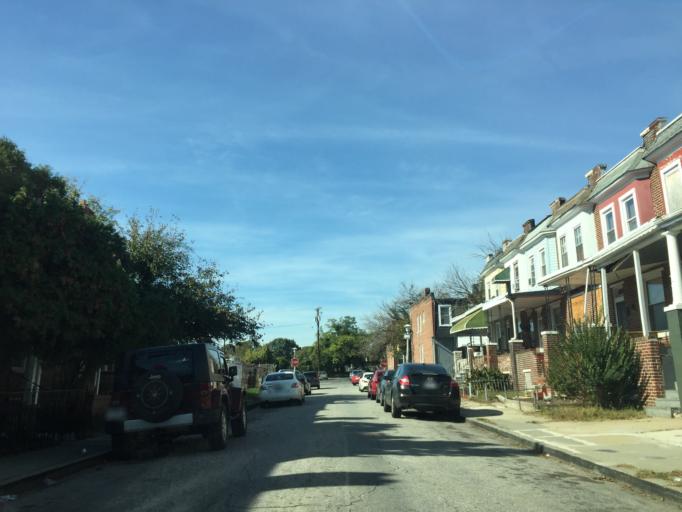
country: US
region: Maryland
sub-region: Baltimore County
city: Lansdowne
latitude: 39.2926
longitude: -76.6639
